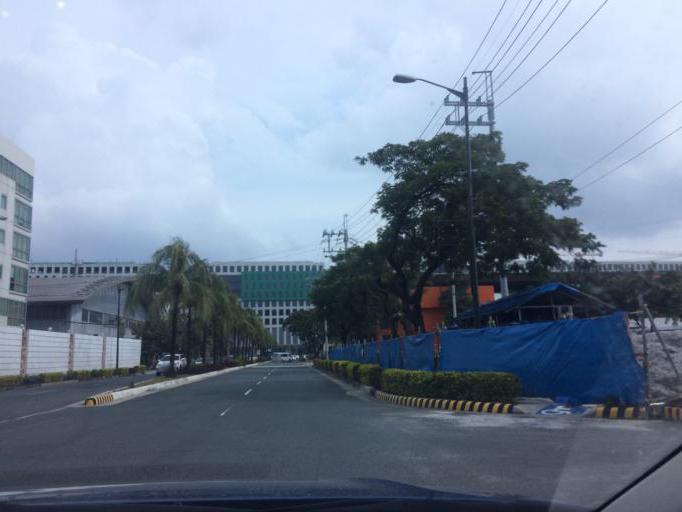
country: PH
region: Metro Manila
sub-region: Makati City
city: Makati City
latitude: 14.5388
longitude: 120.9907
